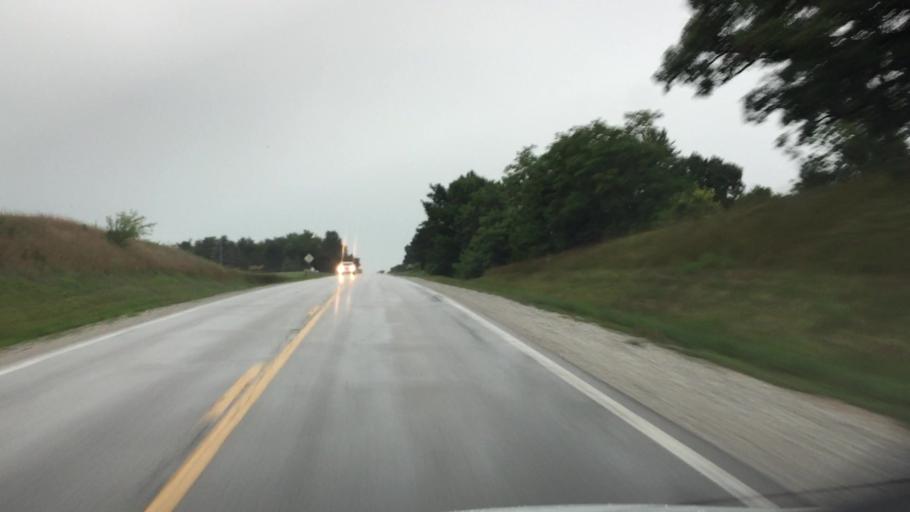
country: US
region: Illinois
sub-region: Hancock County
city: Carthage
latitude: 40.4325
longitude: -91.1401
